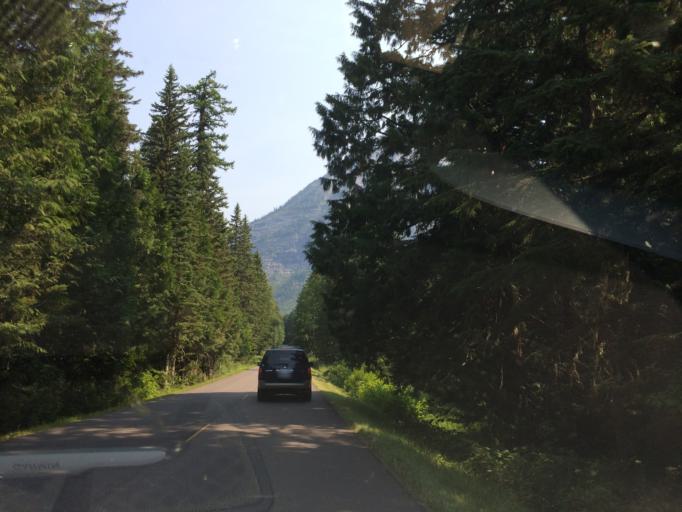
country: US
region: Montana
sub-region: Flathead County
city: Columbia Falls
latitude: 48.6675
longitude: -113.8307
